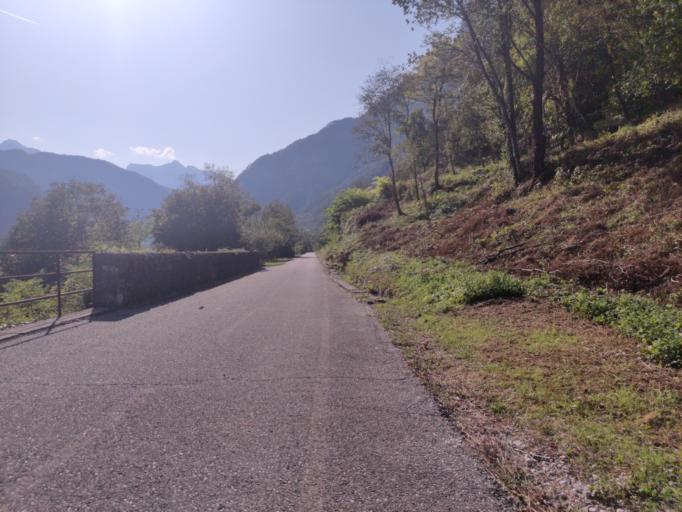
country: IT
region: Friuli Venezia Giulia
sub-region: Provincia di Udine
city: Chiusaforte
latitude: 46.4068
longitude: 13.3007
